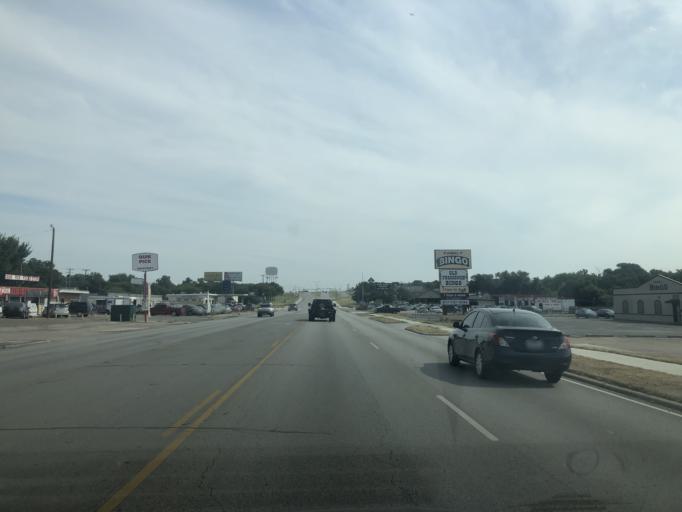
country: US
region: Texas
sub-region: Tarrant County
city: Benbrook
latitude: 32.7087
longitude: -97.4479
